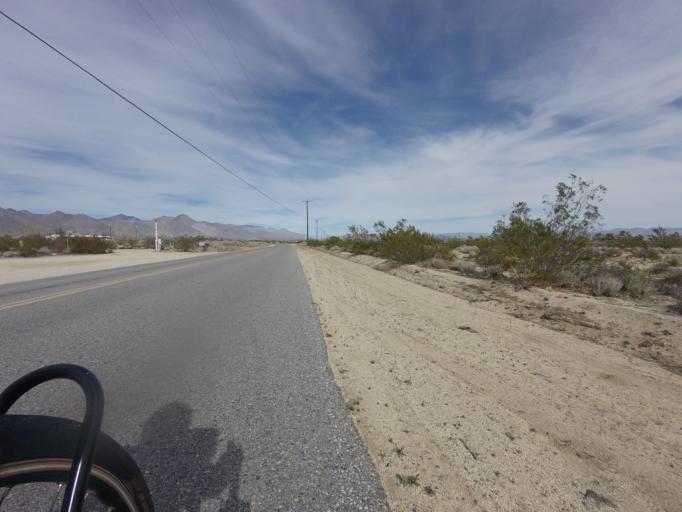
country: US
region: California
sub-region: Kern County
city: Inyokern
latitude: 35.7067
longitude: -117.8301
